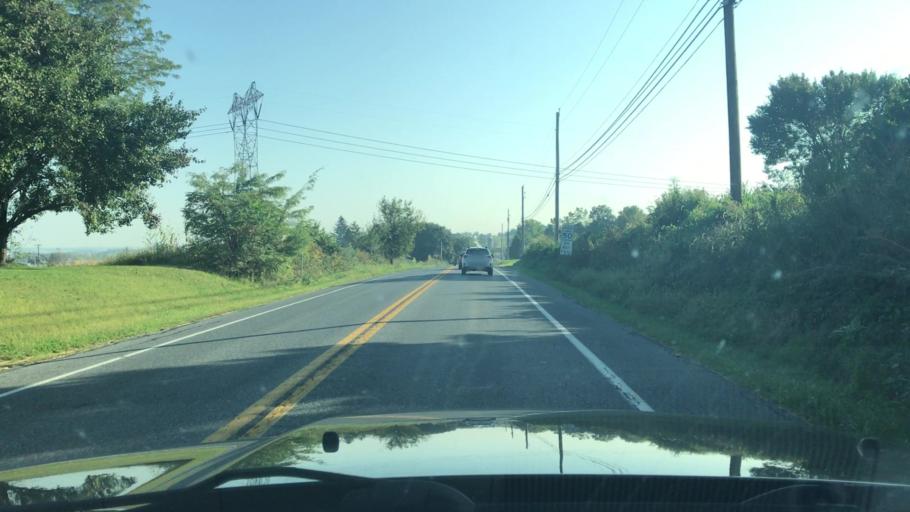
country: US
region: Pennsylvania
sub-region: Berks County
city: Topton
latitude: 40.4865
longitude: -75.7306
